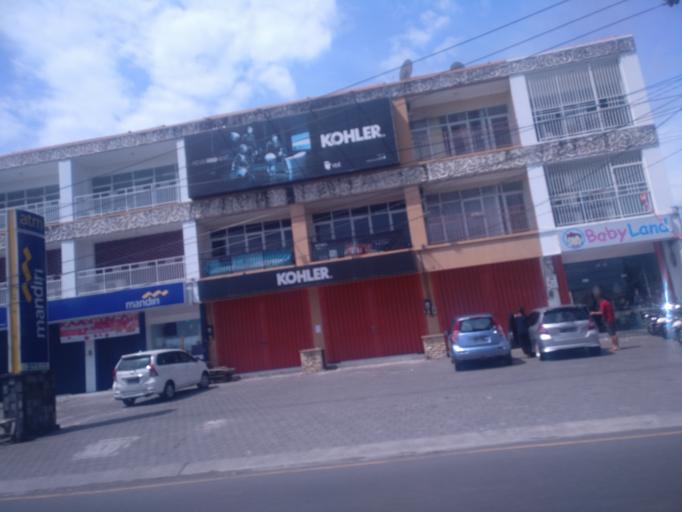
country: ID
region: Bali
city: Banjar Kertasari
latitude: -8.6362
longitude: 115.1940
